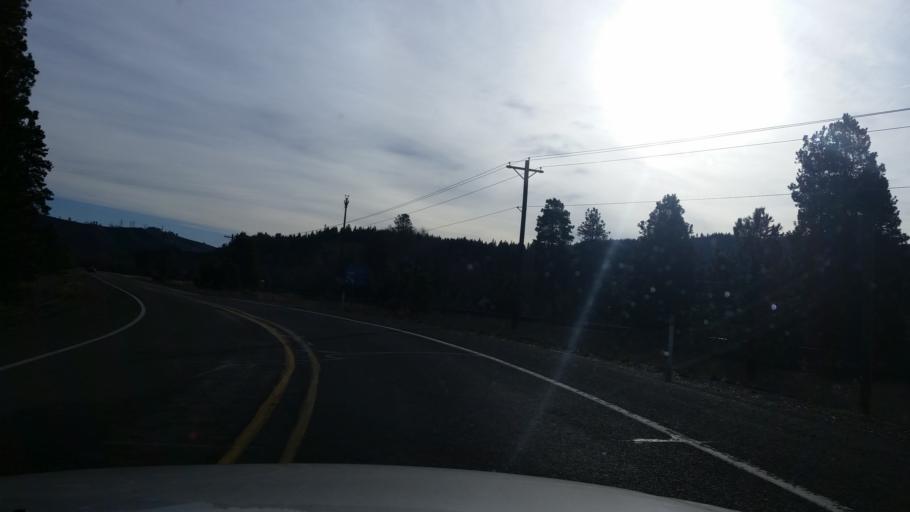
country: US
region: Washington
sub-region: Kittitas County
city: Cle Elum
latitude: 47.1744
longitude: -120.8543
